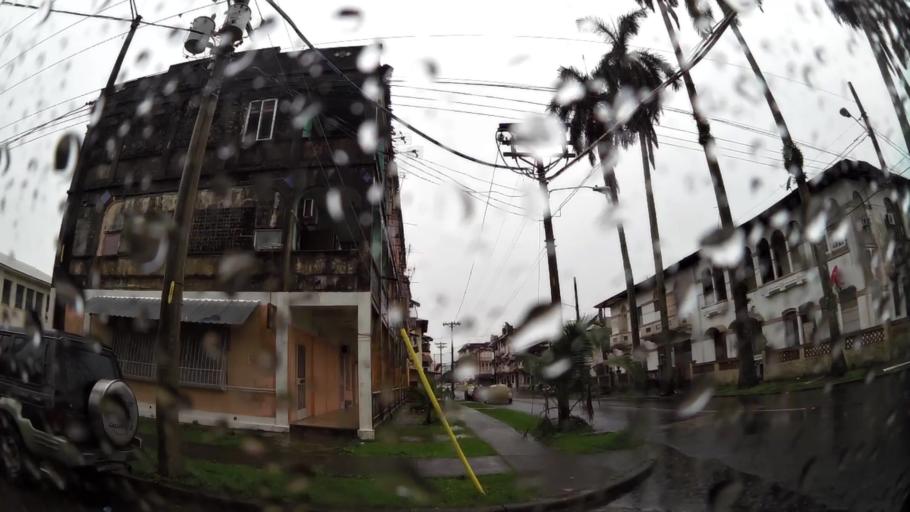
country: PA
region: Colon
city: Colon
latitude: 9.3589
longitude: -79.8976
